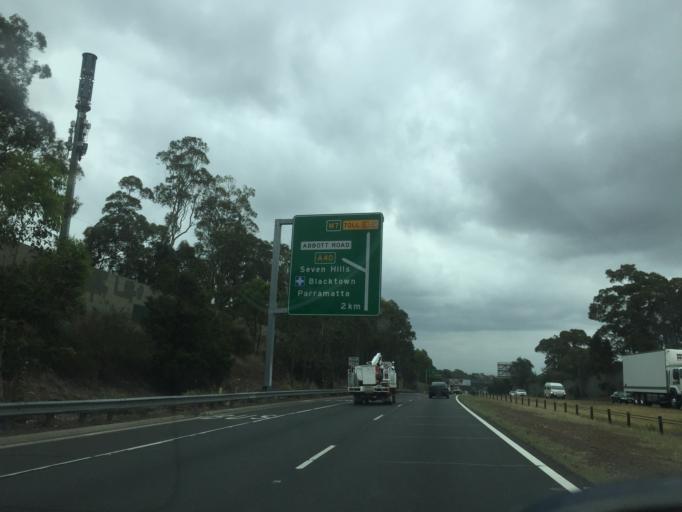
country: AU
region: New South Wales
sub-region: Parramatta
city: Northmead
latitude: -33.7717
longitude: 150.9833
